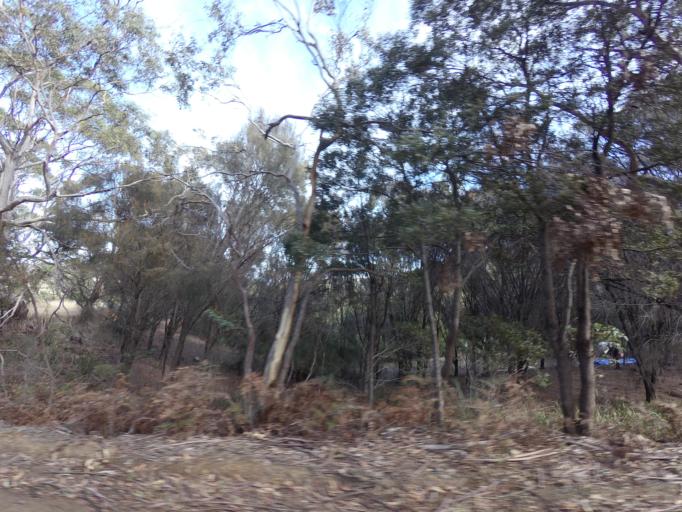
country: AU
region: Tasmania
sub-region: Clarence
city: Sandford
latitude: -43.0821
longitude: 147.6754
